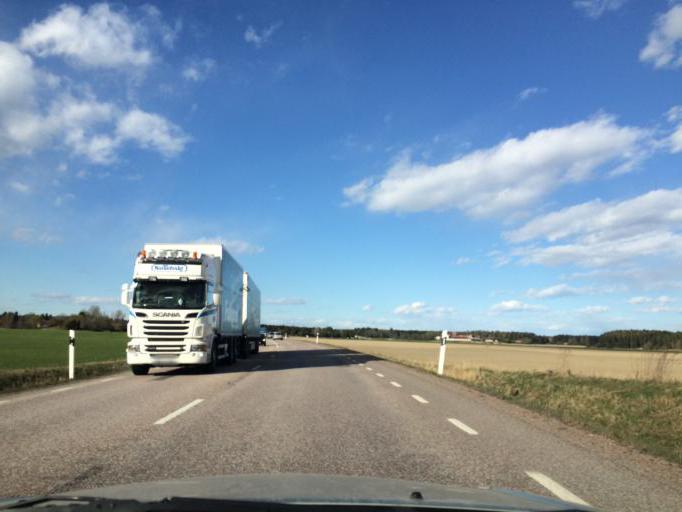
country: SE
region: Vaestmanland
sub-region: Hallstahammars Kommun
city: Kolback
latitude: 59.5523
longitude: 16.3370
